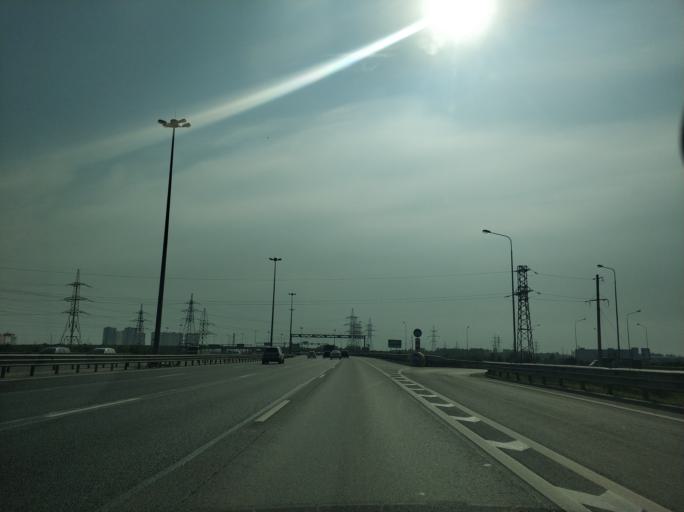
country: RU
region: Leningrad
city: Murino
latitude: 60.0218
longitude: 30.4536
